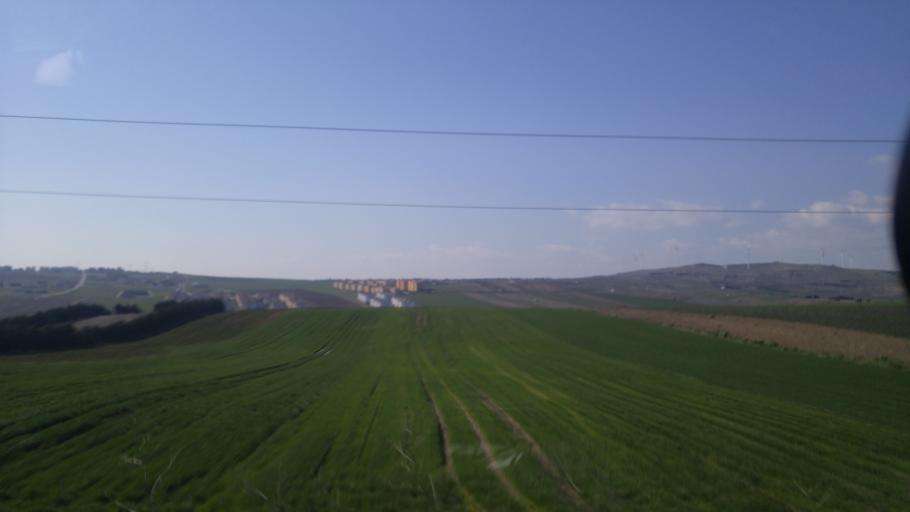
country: TR
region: Istanbul
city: Canta
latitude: 41.0927
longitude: 28.1092
